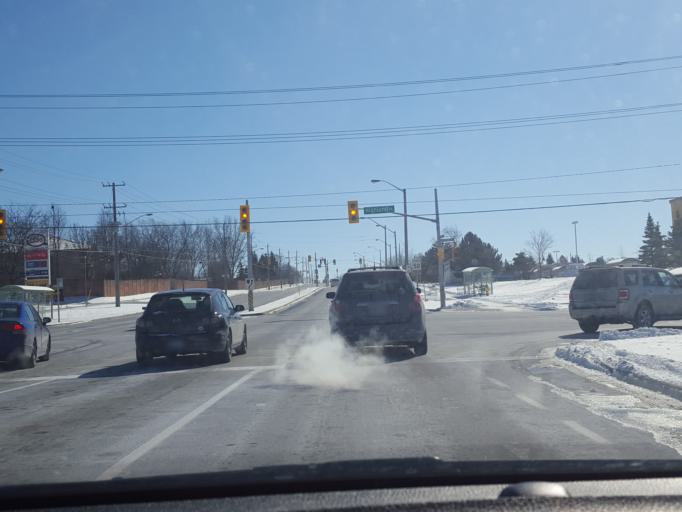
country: CA
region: Ontario
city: Kitchener
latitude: 43.4320
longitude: -80.5258
